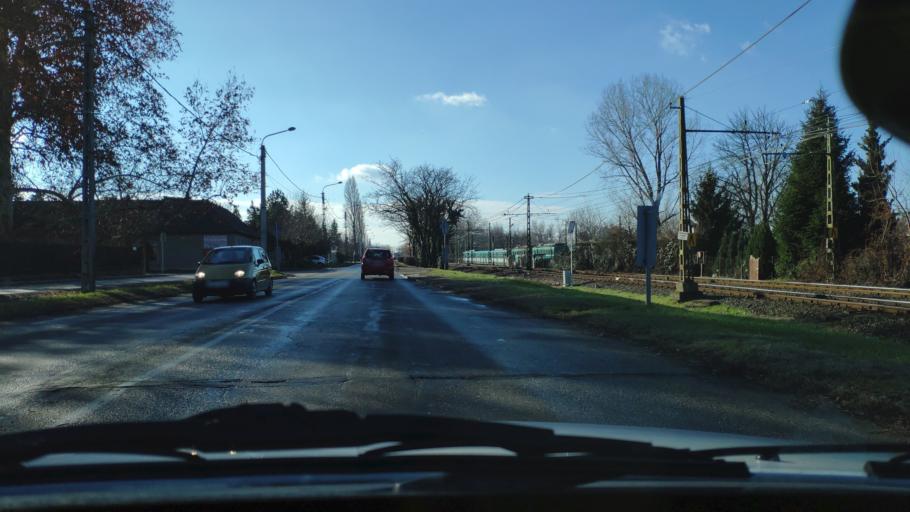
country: HU
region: Pest
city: Dunaharaszti
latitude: 47.3643
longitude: 19.0903
